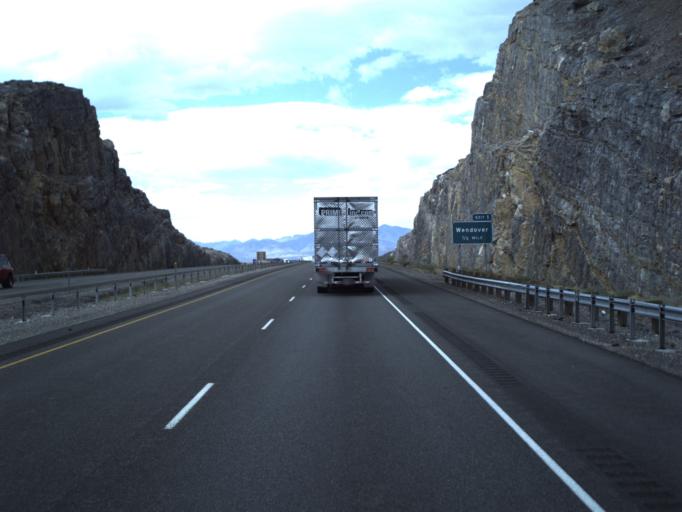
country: US
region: Utah
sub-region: Tooele County
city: Wendover
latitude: 40.7430
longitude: -114.0277
